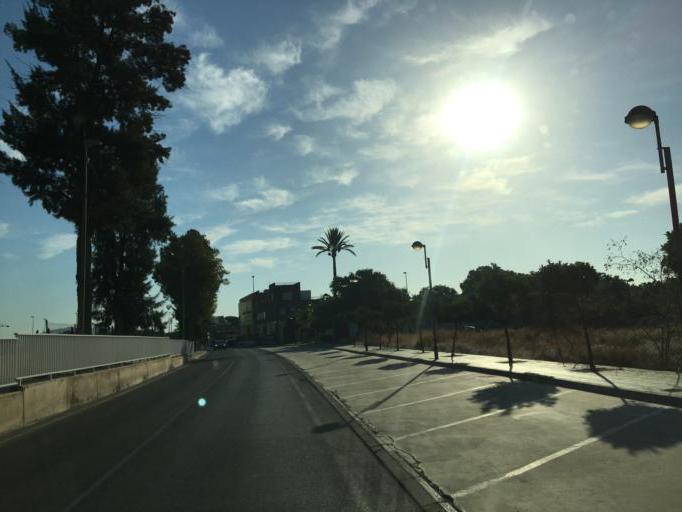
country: ES
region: Murcia
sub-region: Murcia
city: Murcia
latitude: 38.0183
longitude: -1.1433
